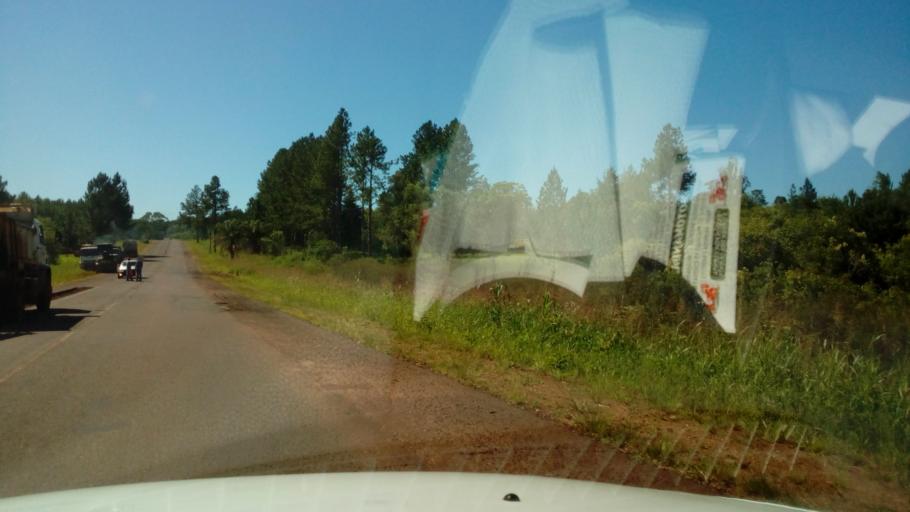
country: AR
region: Misiones
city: Almafuerte
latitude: -27.5516
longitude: -55.4248
